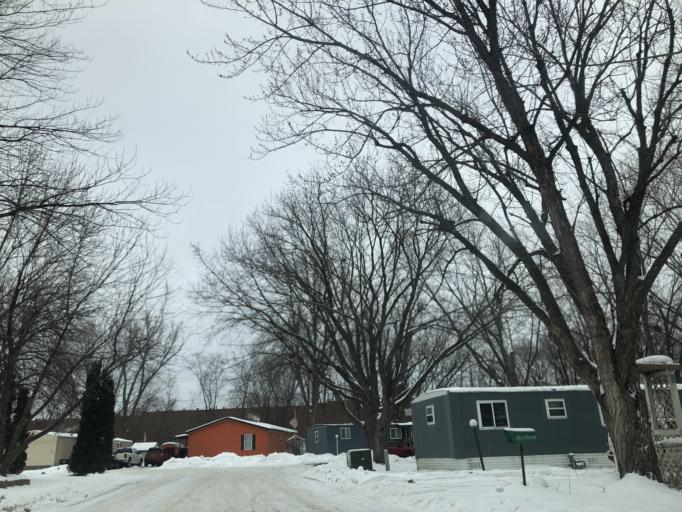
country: US
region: Minnesota
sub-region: Ramsey County
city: New Brighton
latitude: 45.0820
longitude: -93.1818
